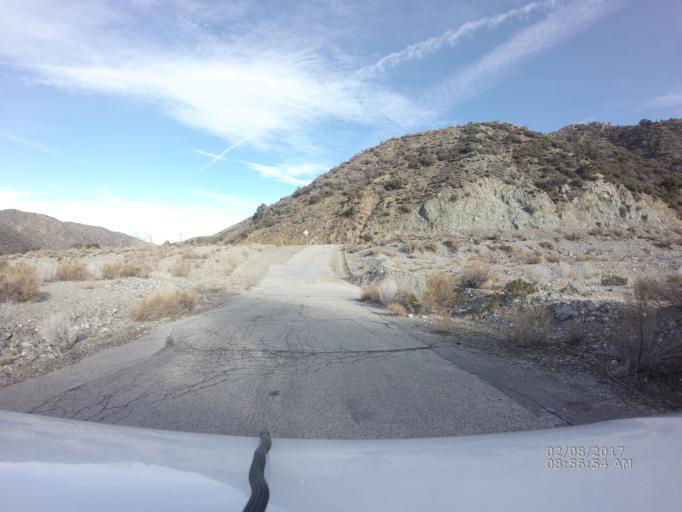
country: US
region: California
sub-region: San Bernardino County
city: Pinon Hills
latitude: 34.3967
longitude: -117.8086
